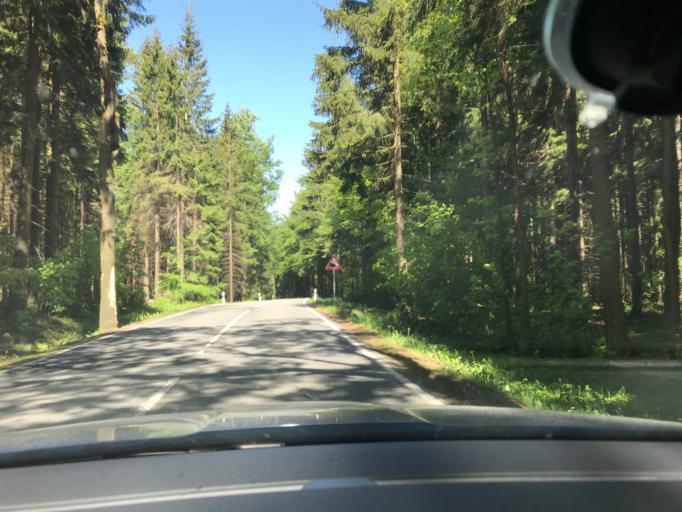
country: DE
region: Saxony
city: Crottendorf
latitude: 50.4941
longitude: 12.9546
